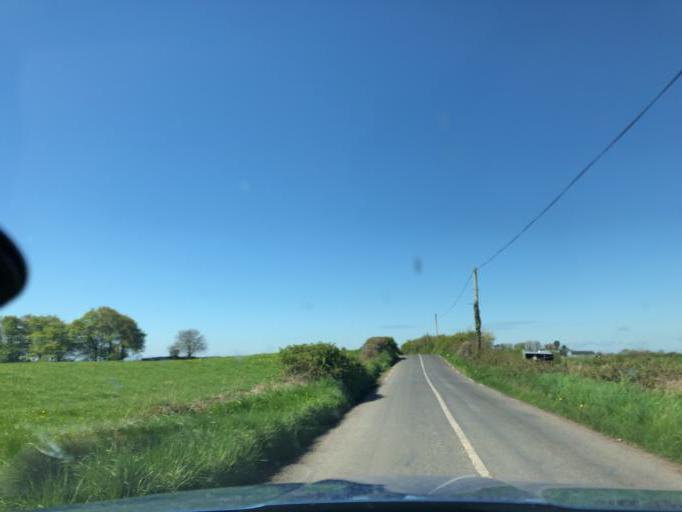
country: IE
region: Connaught
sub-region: County Galway
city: Portumna
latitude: 53.1660
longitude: -8.2198
